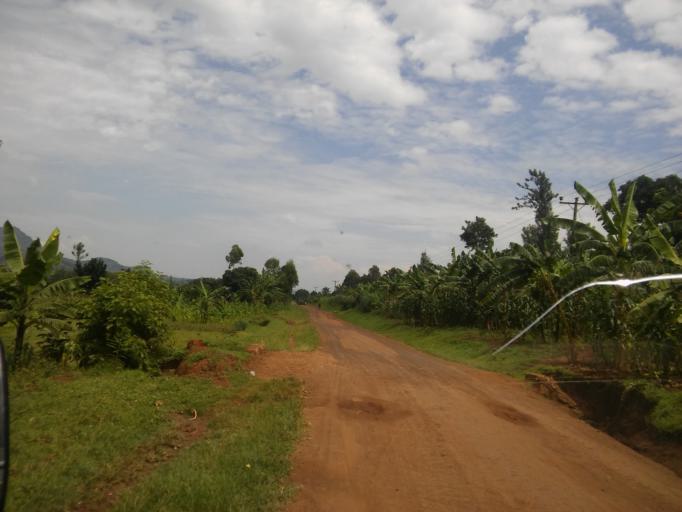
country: UG
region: Eastern Region
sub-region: Bududa District
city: Bududa
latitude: 0.9173
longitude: 34.2780
